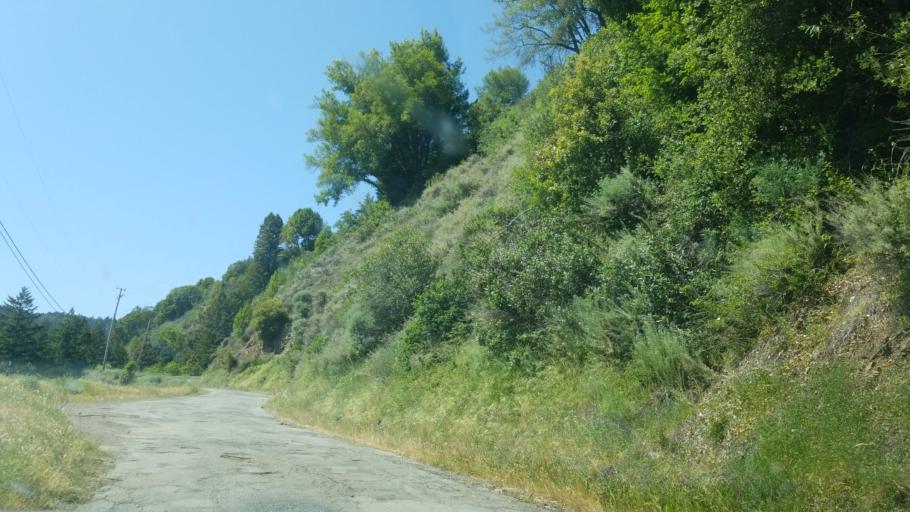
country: US
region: California
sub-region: Santa Cruz County
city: Day Valley
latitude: 37.0627
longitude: -121.8265
